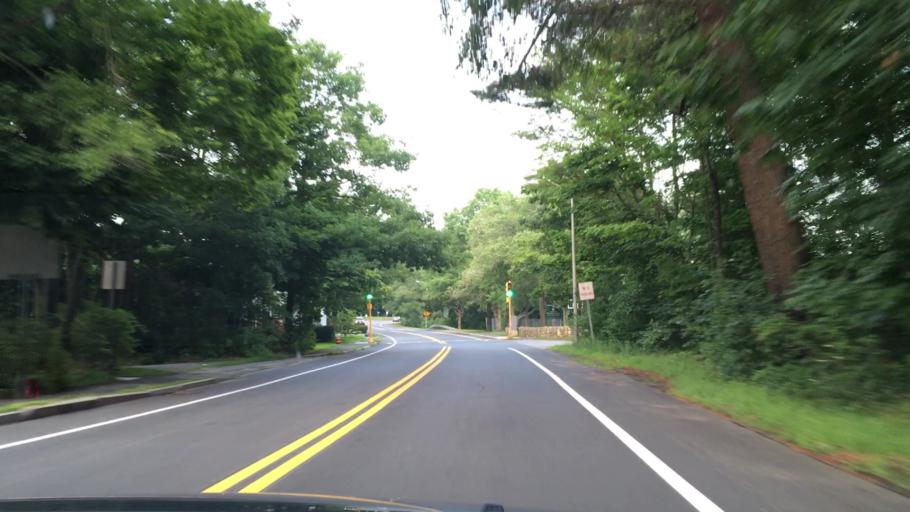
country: US
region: Massachusetts
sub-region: Essex County
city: Essex
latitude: 42.5792
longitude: -70.7603
